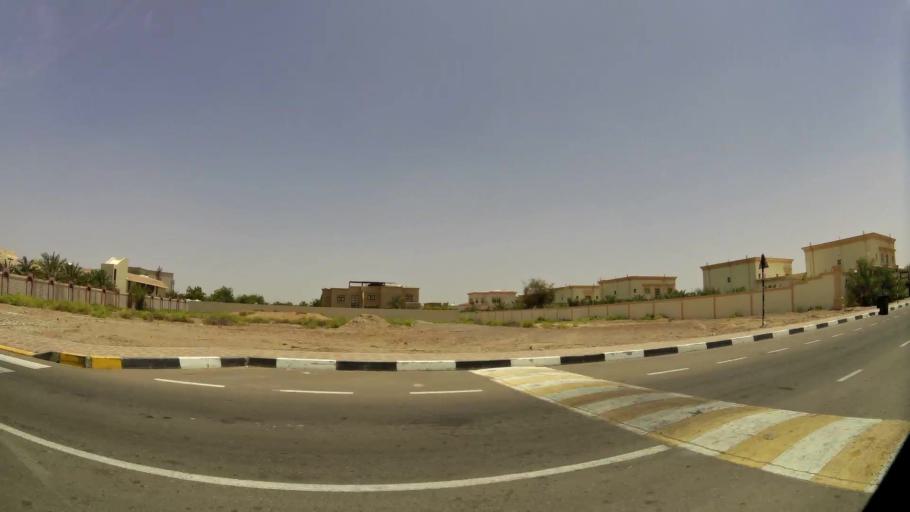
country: OM
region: Al Buraimi
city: Al Buraymi
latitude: 24.2636
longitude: 55.7170
